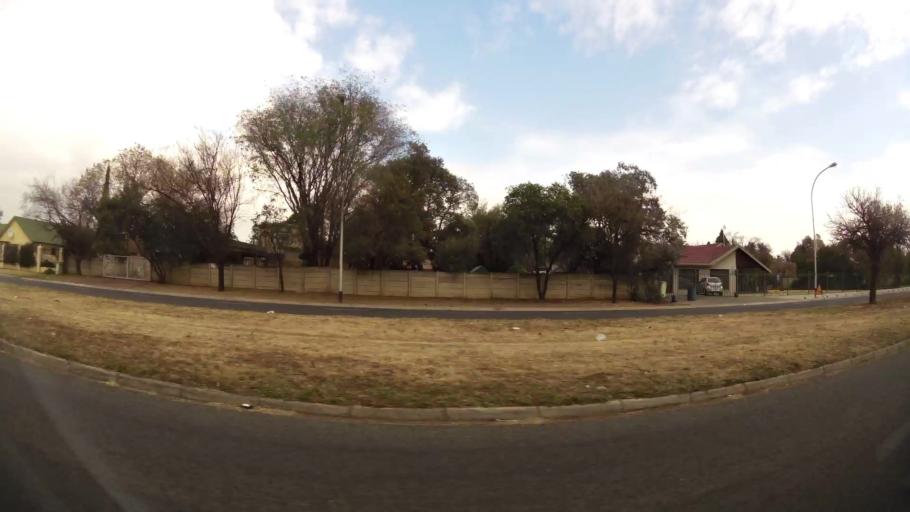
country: ZA
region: Orange Free State
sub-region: Mangaung Metropolitan Municipality
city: Bloemfontein
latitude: -29.1195
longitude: 26.1648
